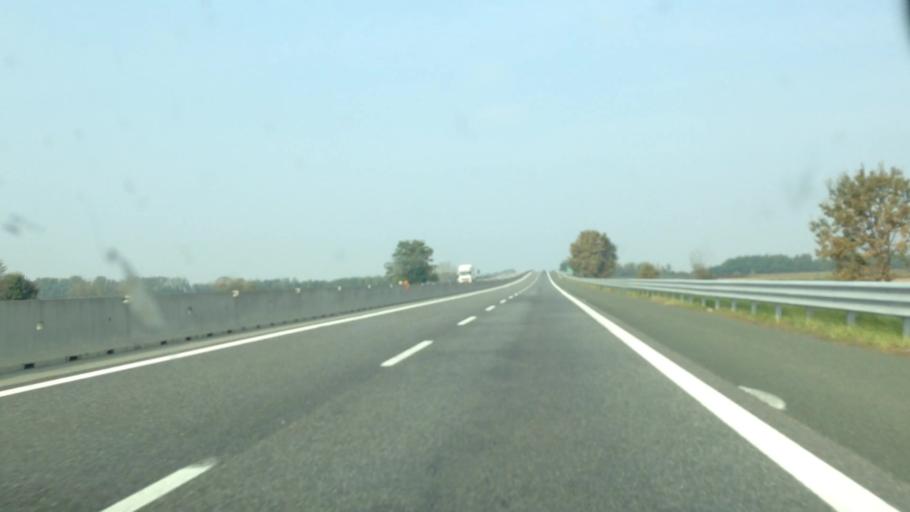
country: IT
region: Piedmont
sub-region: Provincia di Vercelli
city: Crova
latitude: 45.3345
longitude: 8.2223
